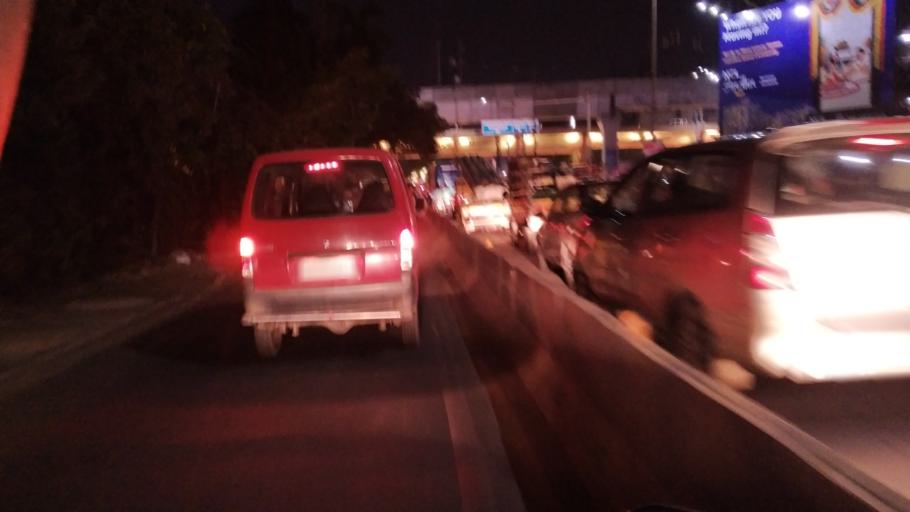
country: IN
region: Telangana
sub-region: Hyderabad
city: Malkajgiri
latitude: 17.4445
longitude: 78.4875
